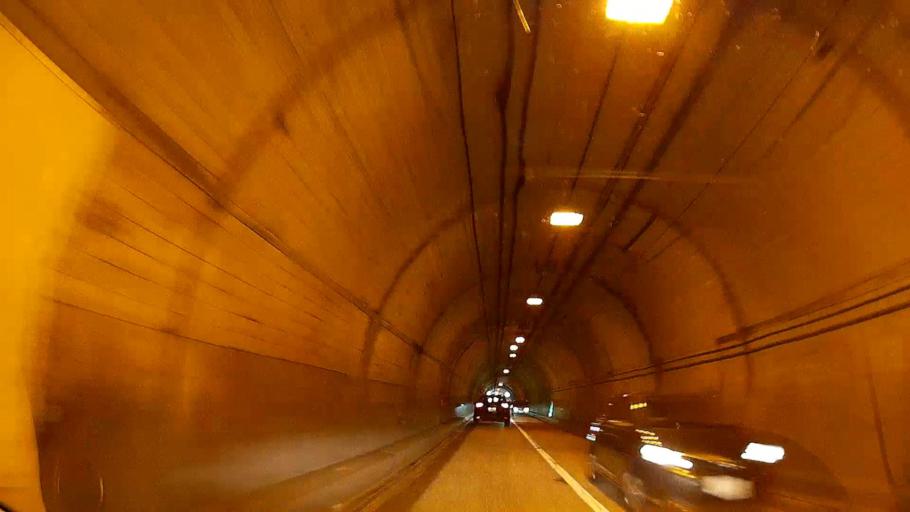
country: JP
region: Nagano
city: Toyoshina
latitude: 36.1371
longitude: 137.7074
